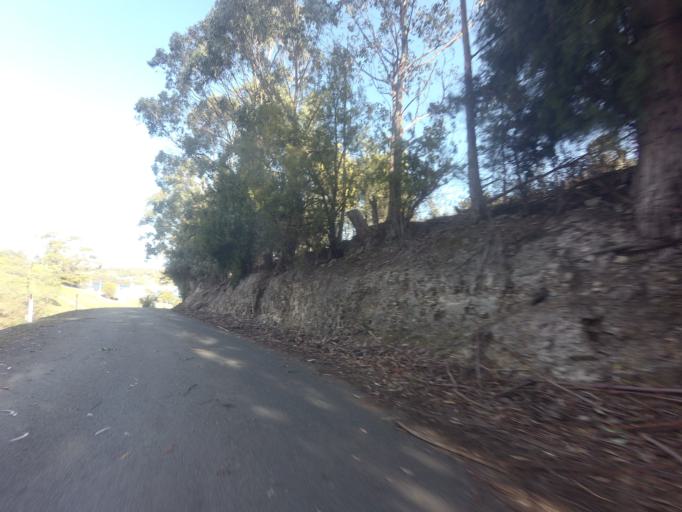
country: AU
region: Tasmania
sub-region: Kingborough
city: Kettering
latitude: -43.1199
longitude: 147.2561
